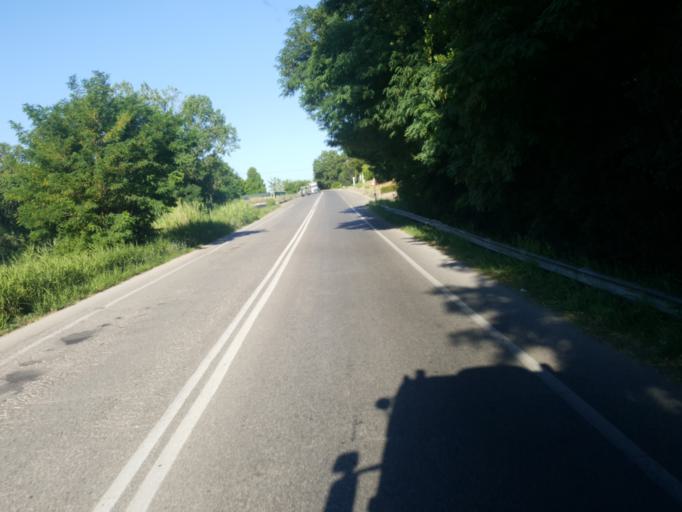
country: IT
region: The Marches
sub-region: Provincia di Pesaro e Urbino
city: Montelabbate
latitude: 43.8457
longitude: 12.7767
